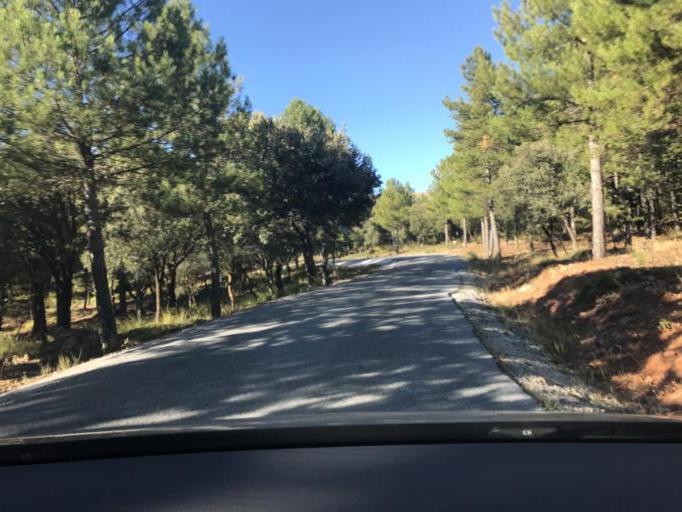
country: ES
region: Andalusia
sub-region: Provincia de Granada
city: Beas de Granada
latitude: 37.3035
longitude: -3.4439
